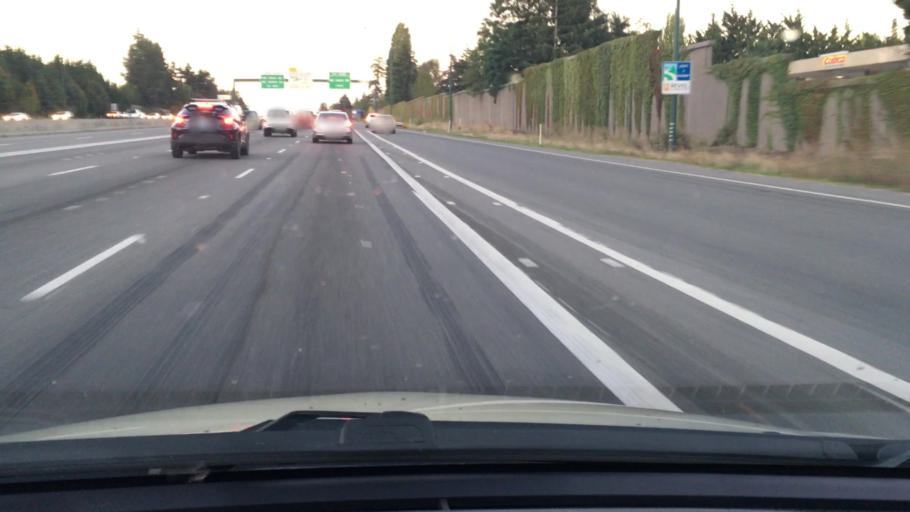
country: US
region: Washington
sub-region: King County
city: Kirkland
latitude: 47.6841
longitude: -122.1855
